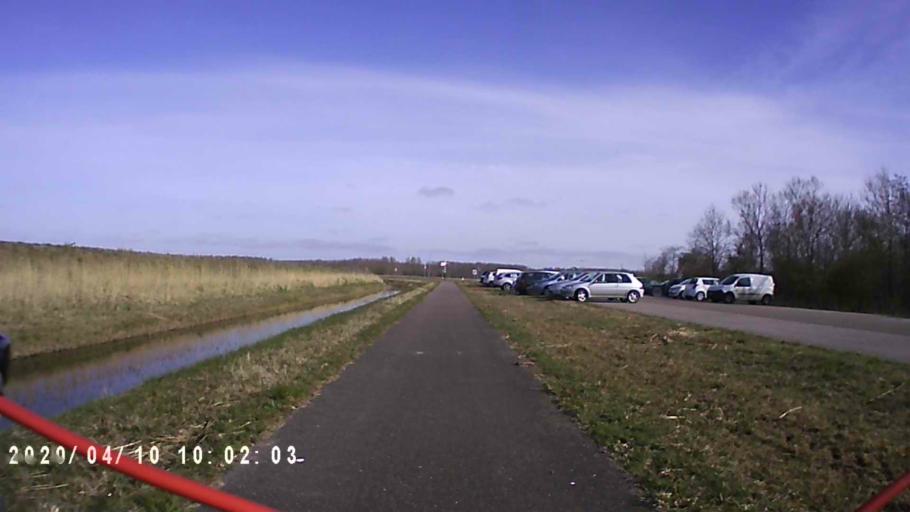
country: NL
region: Groningen
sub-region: Gemeente De Marne
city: Ulrum
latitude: 53.3635
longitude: 6.2605
